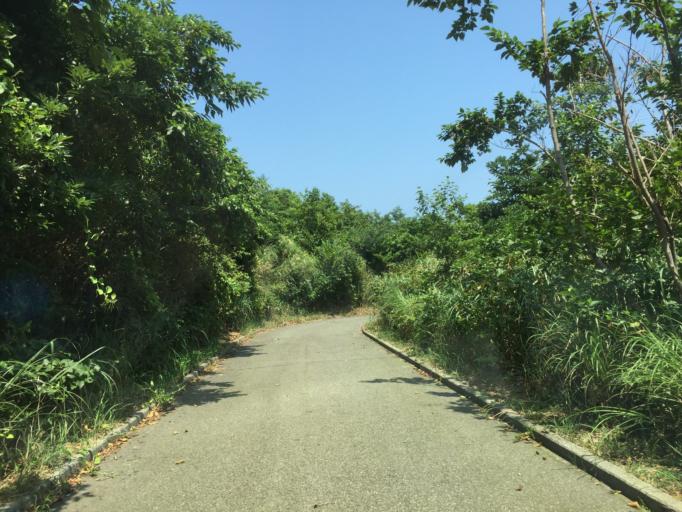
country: JP
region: Shizuoka
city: Shimoda
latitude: 34.0999
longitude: 139.5486
